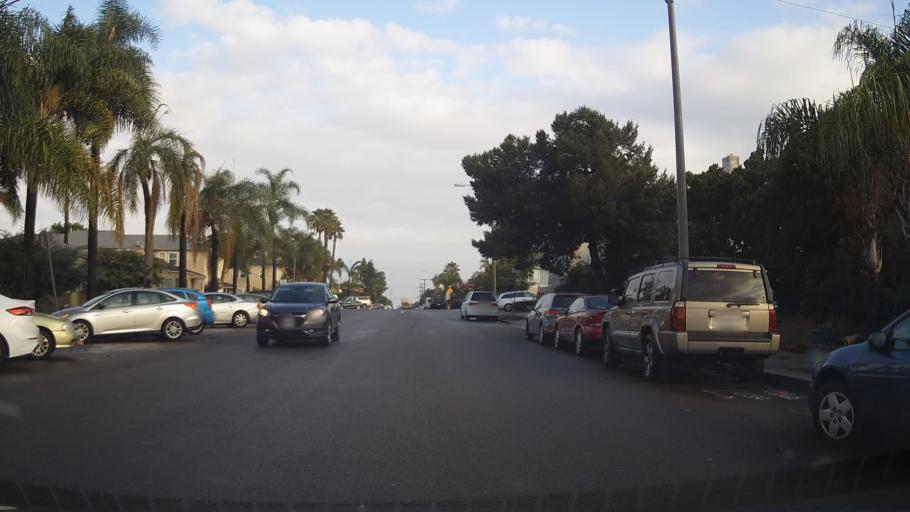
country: US
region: California
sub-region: San Diego County
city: San Diego
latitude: 32.7566
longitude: -117.1288
